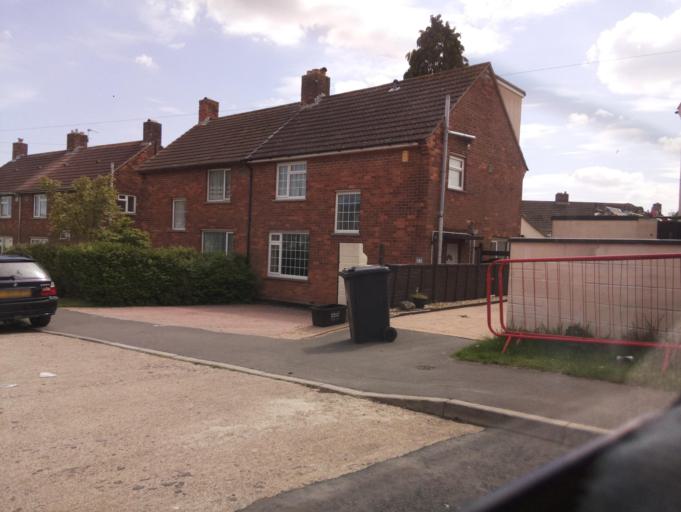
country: GB
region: England
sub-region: Bristol
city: Bristol
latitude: 51.5075
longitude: -2.6030
